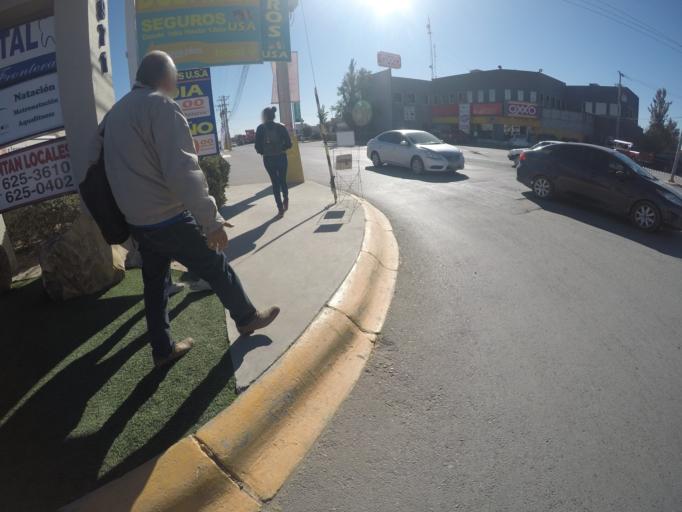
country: US
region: Texas
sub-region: El Paso County
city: Socorro
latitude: 31.6942
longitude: -106.3744
